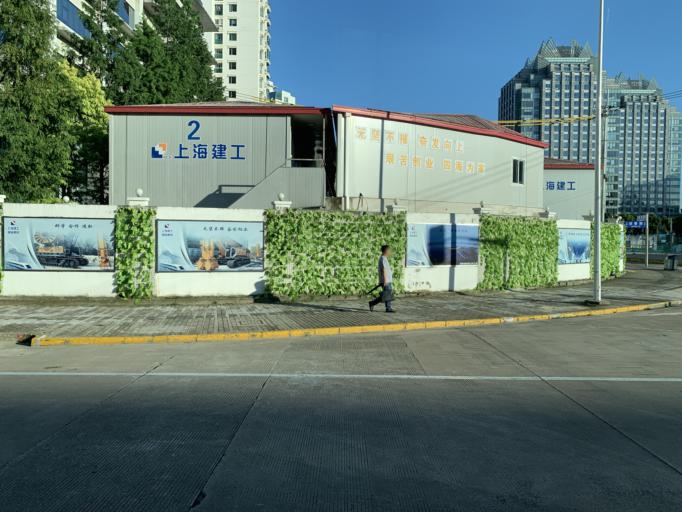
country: CN
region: Shanghai Shi
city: Huamu
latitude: 31.2250
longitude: 121.5464
